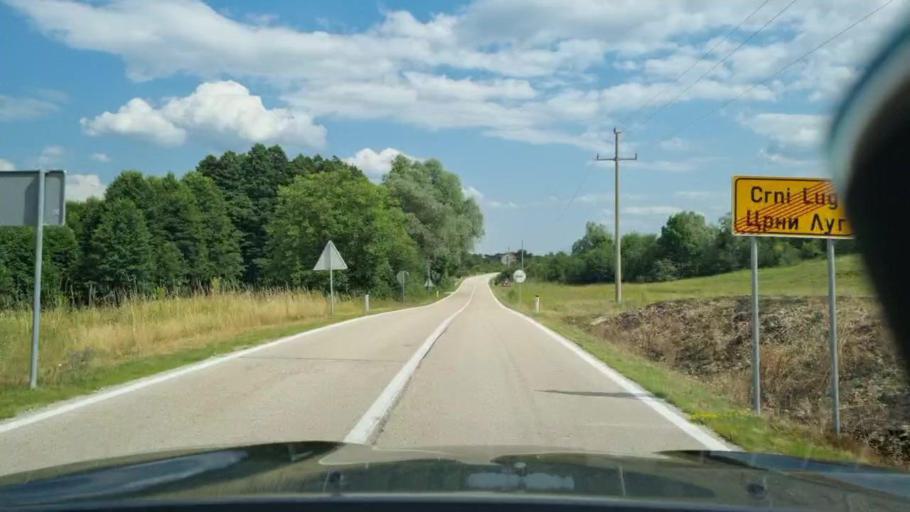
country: BA
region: Federation of Bosnia and Herzegovina
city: Bosansko Grahovo
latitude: 44.0738
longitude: 16.5730
